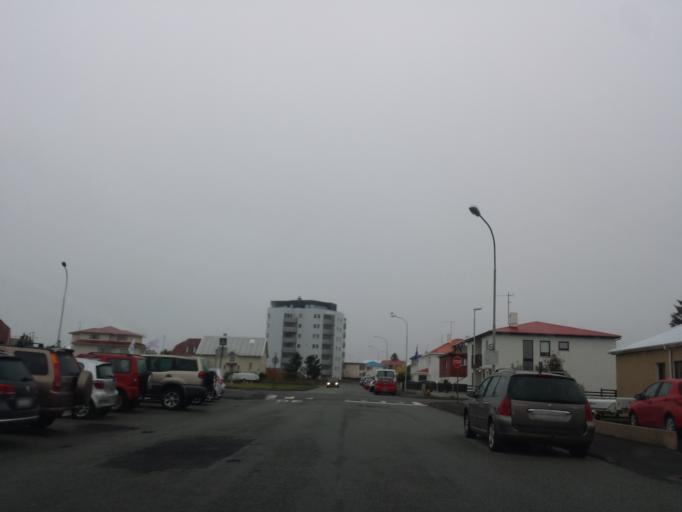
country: IS
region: Southern Peninsula
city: Reykjanesbaer
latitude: 64.0008
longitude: -22.5561
